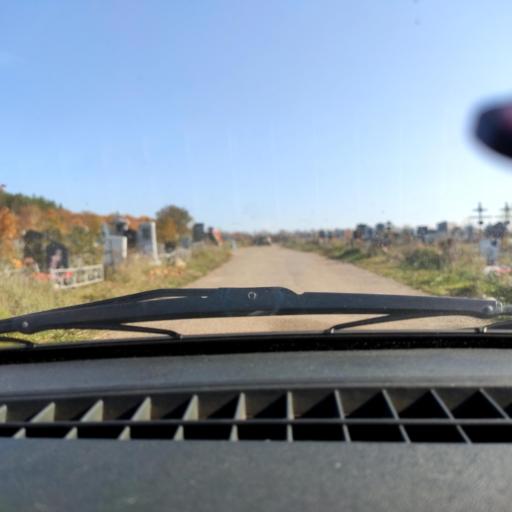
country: RU
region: Bashkortostan
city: Mikhaylovka
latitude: 54.8180
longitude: 55.8674
